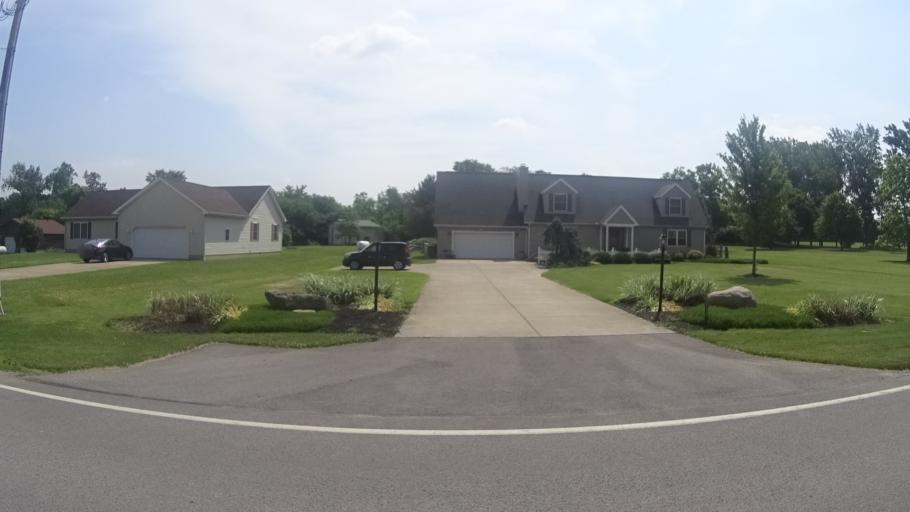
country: US
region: Ohio
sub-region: Erie County
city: Sandusky
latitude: 41.3593
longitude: -82.7279
